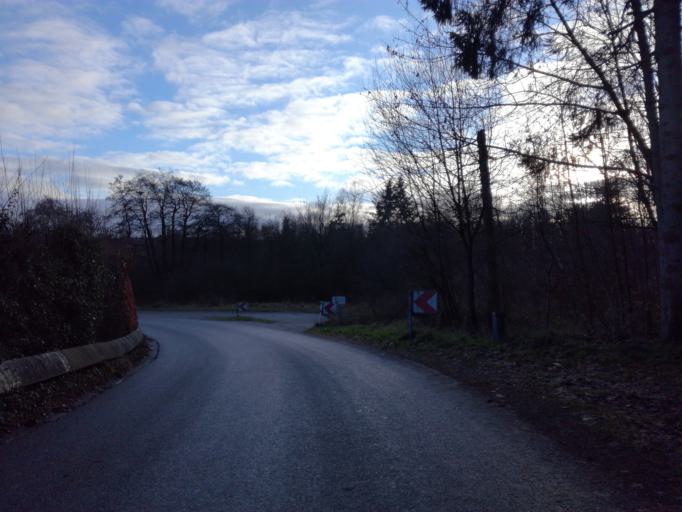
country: DK
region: South Denmark
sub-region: Fredericia Kommune
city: Taulov
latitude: 55.5499
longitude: 9.6012
